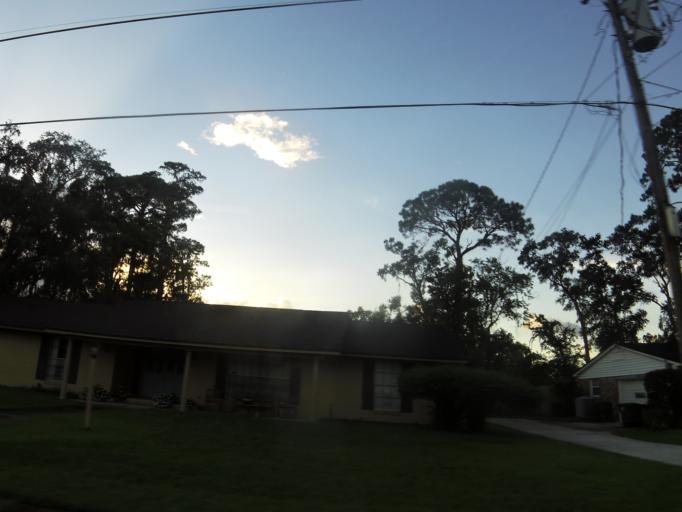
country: US
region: Florida
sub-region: Duval County
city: Jacksonville
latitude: 30.2381
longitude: -81.6233
